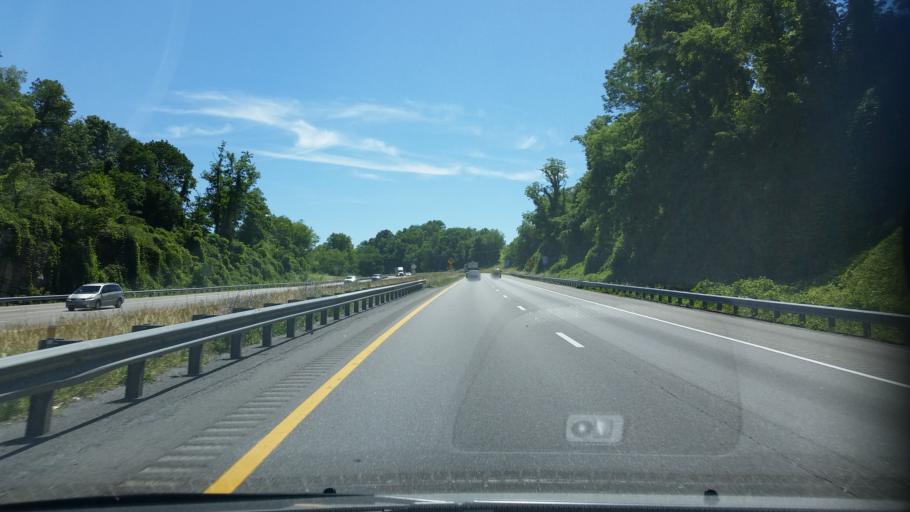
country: US
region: Virginia
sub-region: Smyth County
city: Marion
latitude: 36.8521
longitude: -81.4778
